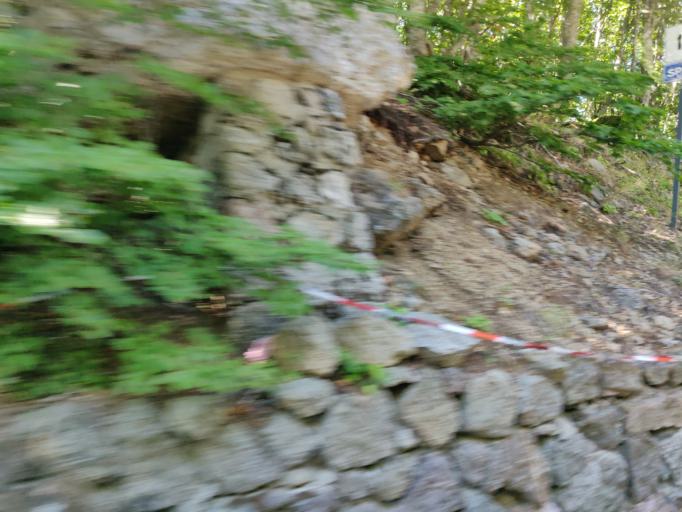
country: IT
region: Tuscany
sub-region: Provincia di Siena
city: Abbadia San Salvatore
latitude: 42.8905
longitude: 11.6284
